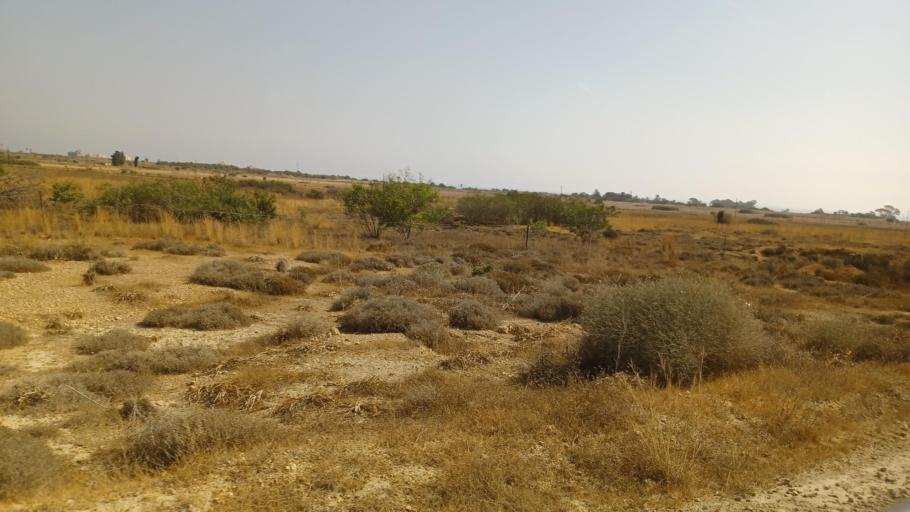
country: CY
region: Ammochostos
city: Deryneia
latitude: 35.0665
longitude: 33.9768
